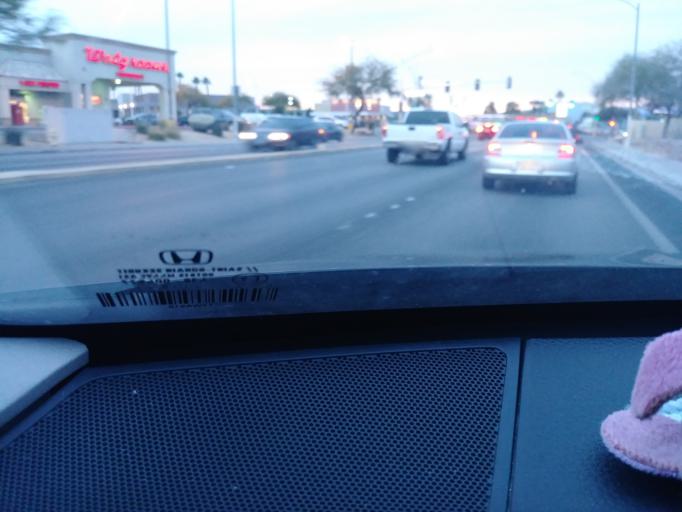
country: US
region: Nevada
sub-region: Clark County
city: Spring Valley
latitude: 36.1583
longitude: -115.2347
